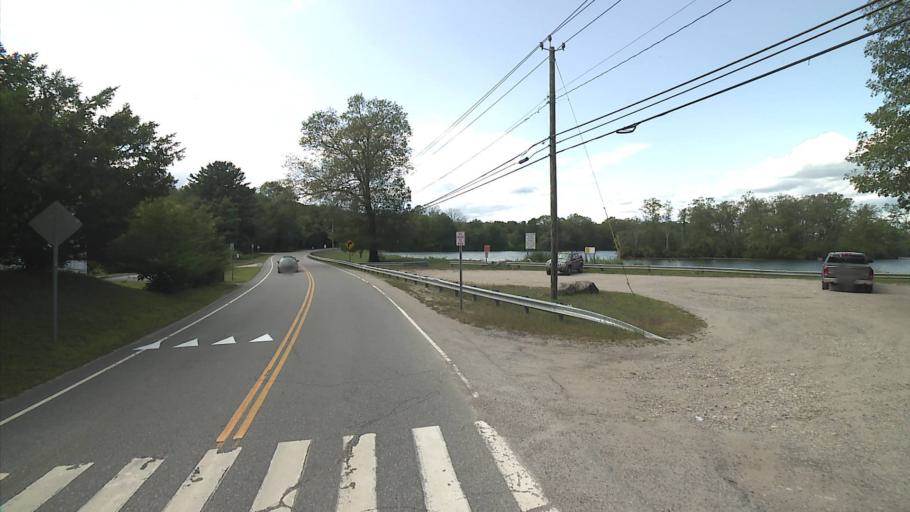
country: US
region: Connecticut
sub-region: New London County
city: Colchester
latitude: 41.6296
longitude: -72.3007
